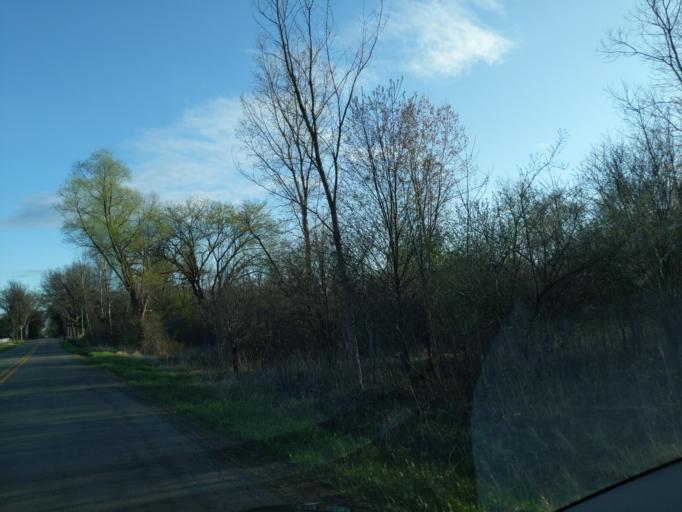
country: US
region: Michigan
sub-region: Jackson County
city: Jackson
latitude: 42.3269
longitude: -84.4481
